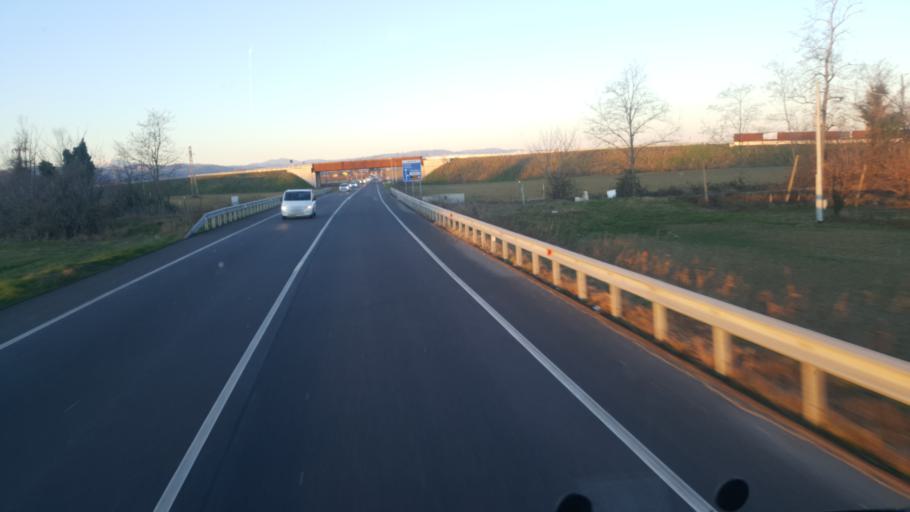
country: IT
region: Emilia-Romagna
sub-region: Provincia di Bologna
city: Bazzano
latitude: 44.5109
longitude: 11.0693
